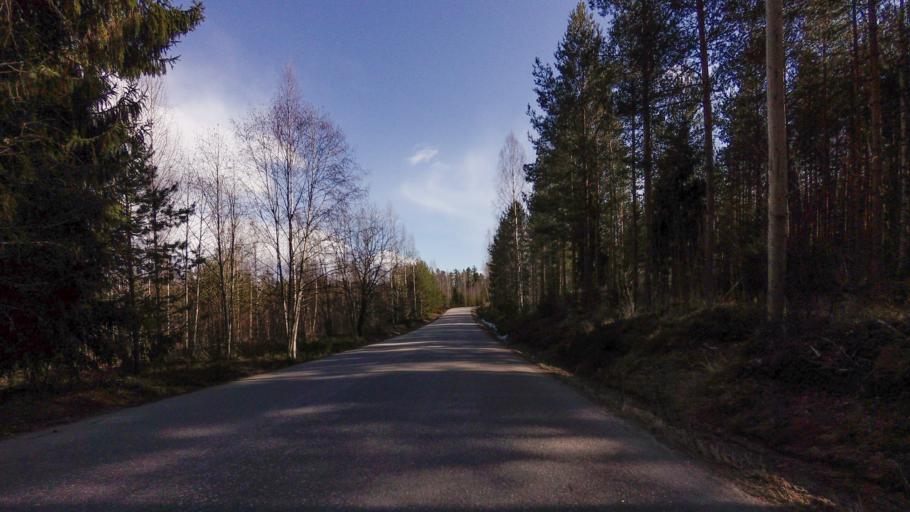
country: FI
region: Varsinais-Suomi
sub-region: Salo
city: Suomusjaervi
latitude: 60.3090
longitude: 23.6448
